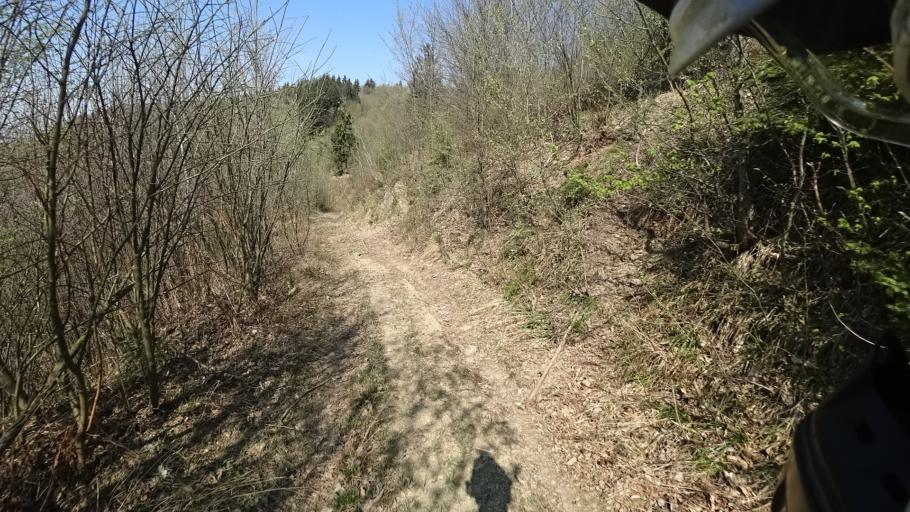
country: HR
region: Zagrebacka
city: Jablanovec
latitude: 45.8905
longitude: 15.9184
